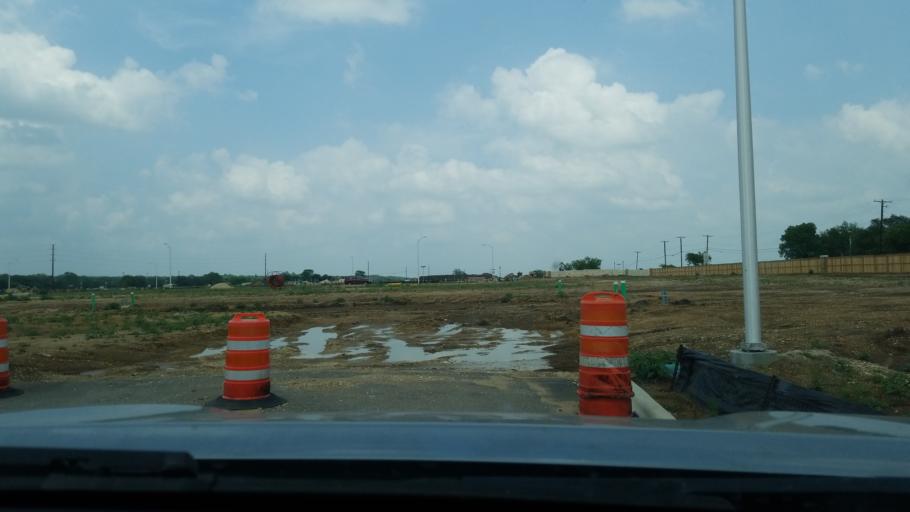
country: US
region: Texas
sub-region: Comal County
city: New Braunfels
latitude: 29.7473
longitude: -98.0945
